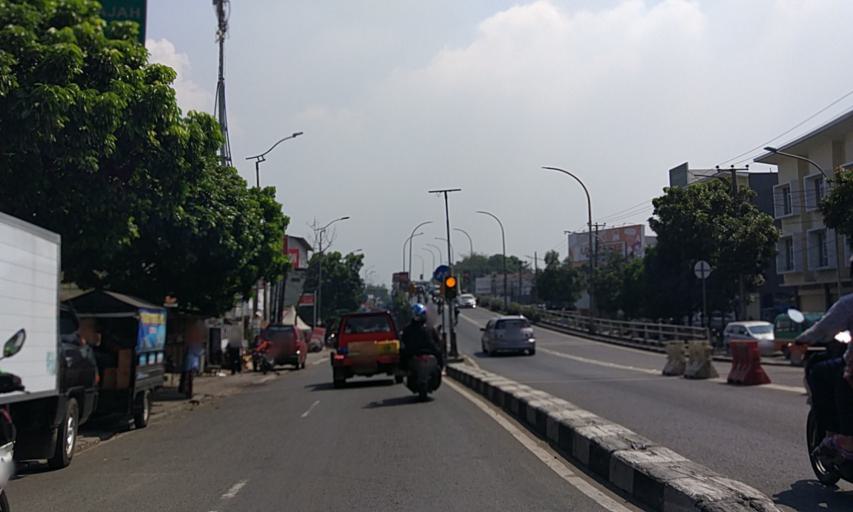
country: ID
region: West Java
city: Cimahi
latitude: -6.8987
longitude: 107.5619
